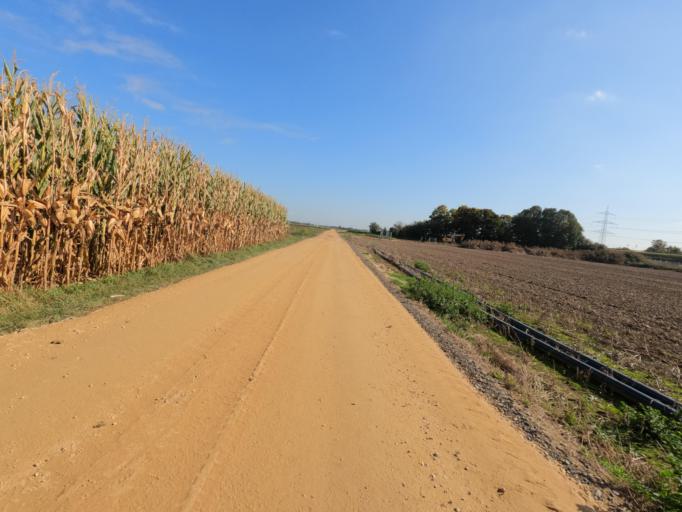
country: DE
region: North Rhine-Westphalia
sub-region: Regierungsbezirk Koln
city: Inden
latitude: 50.8370
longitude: 6.3998
